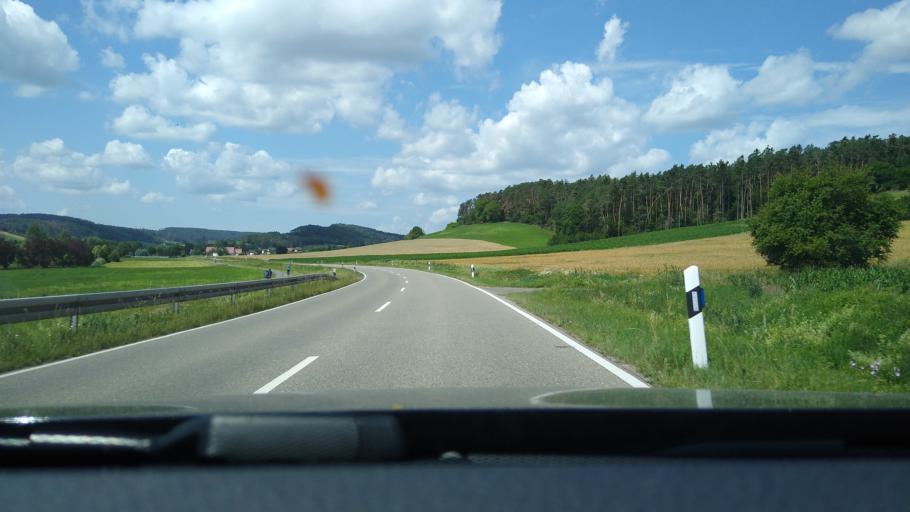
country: DE
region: Bavaria
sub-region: Regierungsbezirk Mittelfranken
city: Trautskirchen
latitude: 49.4563
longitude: 10.6172
